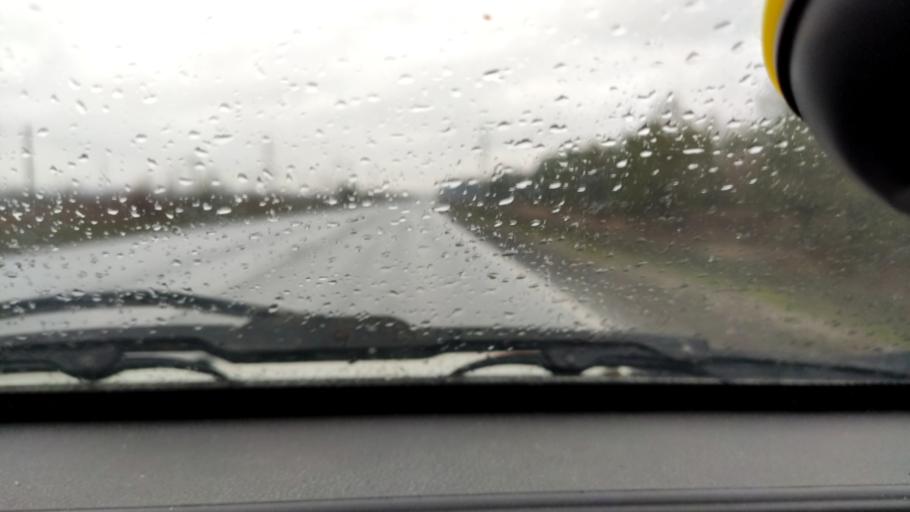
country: RU
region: Samara
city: Zhigulevsk
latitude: 53.5725
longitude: 49.5533
